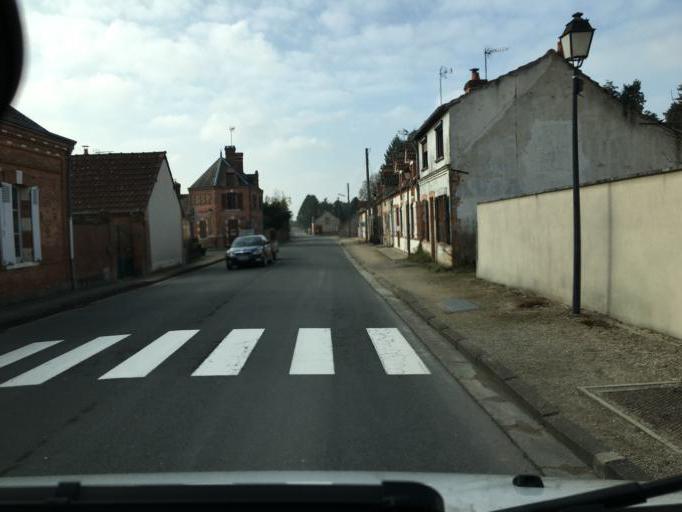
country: FR
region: Centre
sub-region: Departement du Loiret
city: Ligny-le-Ribault
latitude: 47.6230
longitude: 1.7546
